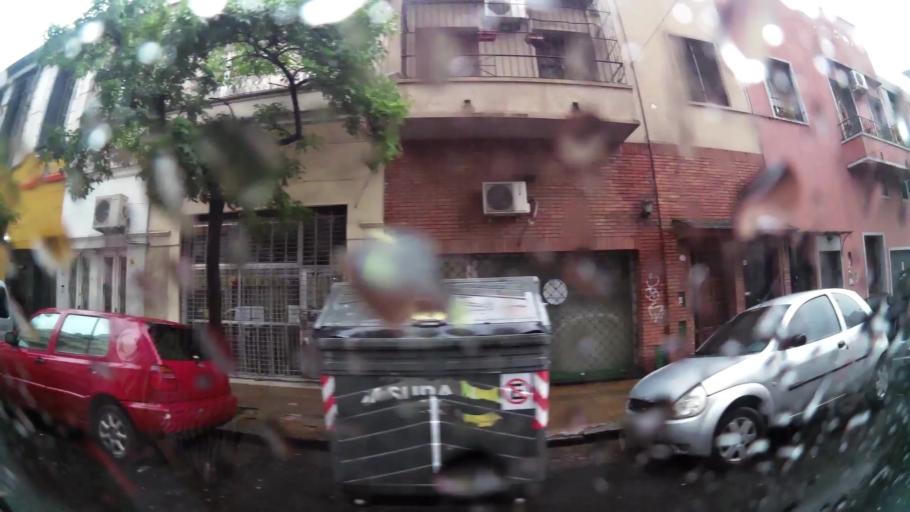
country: AR
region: Buenos Aires
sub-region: Partido de Avellaneda
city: Avellaneda
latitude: -34.6379
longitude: -58.3757
